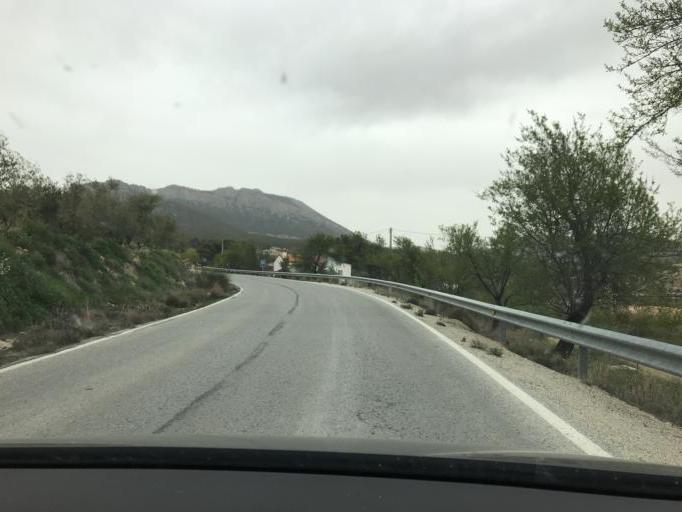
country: ES
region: Andalusia
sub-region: Provincia de Granada
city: Castril
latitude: 37.8143
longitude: -2.7639
